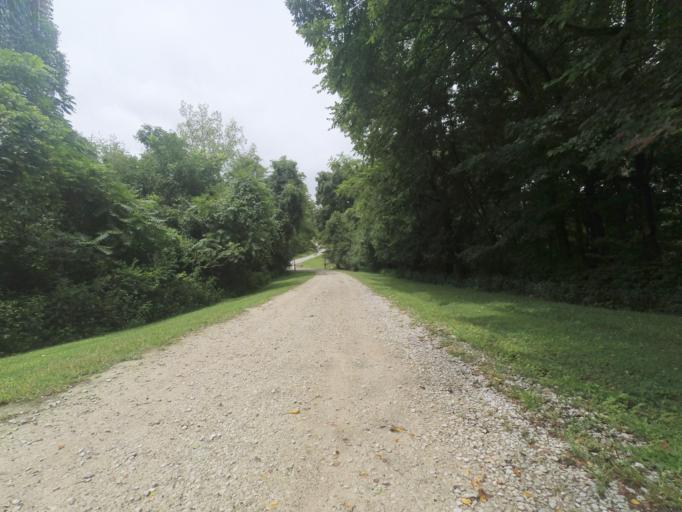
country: US
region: West Virginia
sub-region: Cabell County
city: Huntington
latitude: 38.4320
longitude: -82.4681
